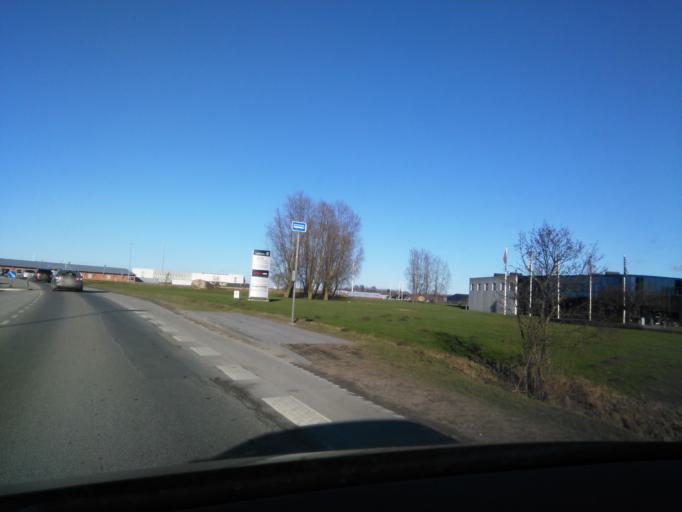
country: DK
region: North Denmark
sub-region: Mariagerfjord Kommune
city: Hobro
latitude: 56.6517
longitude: 9.7952
